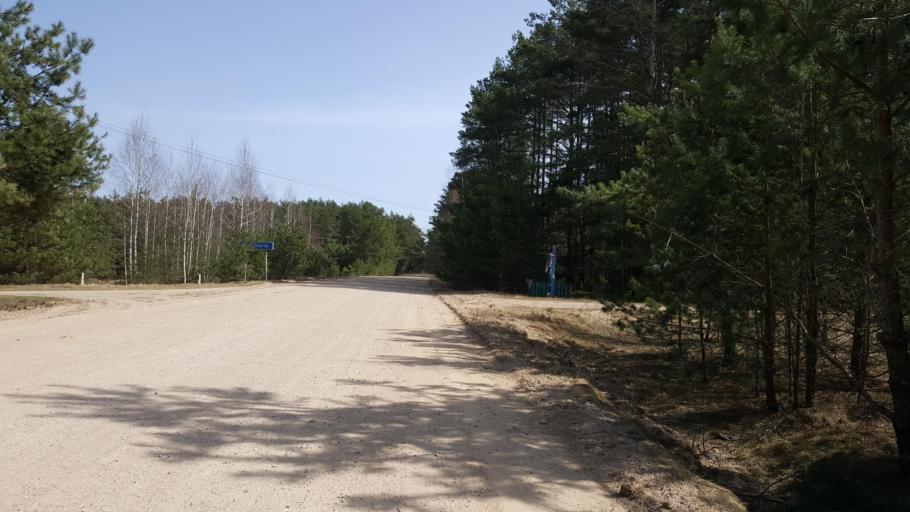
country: BY
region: Brest
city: Kamyanyuki
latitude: 52.5633
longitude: 23.7746
